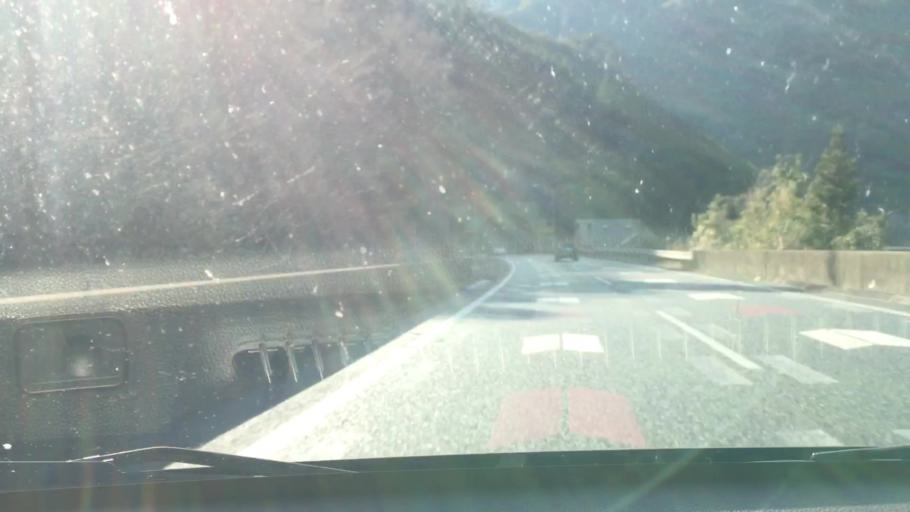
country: JP
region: Kumamoto
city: Hitoyoshi
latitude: 32.3166
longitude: 130.7526
